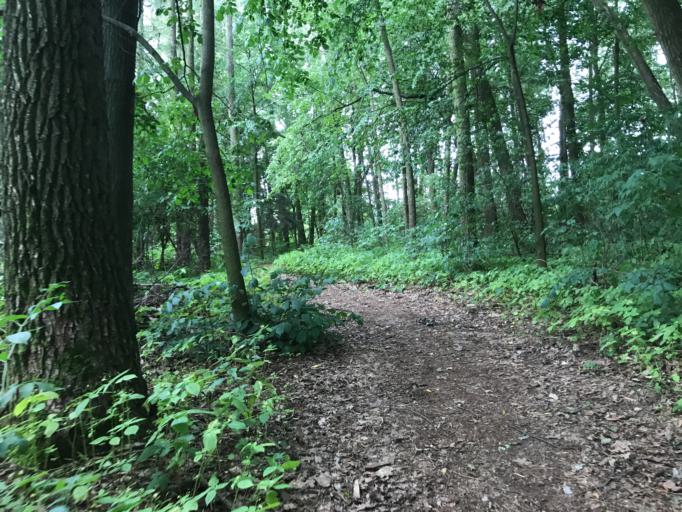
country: CZ
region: Jihocesky
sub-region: Okres Jindrichuv Hradec
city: Lomnice nad Luznici
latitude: 49.0968
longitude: 14.7156
